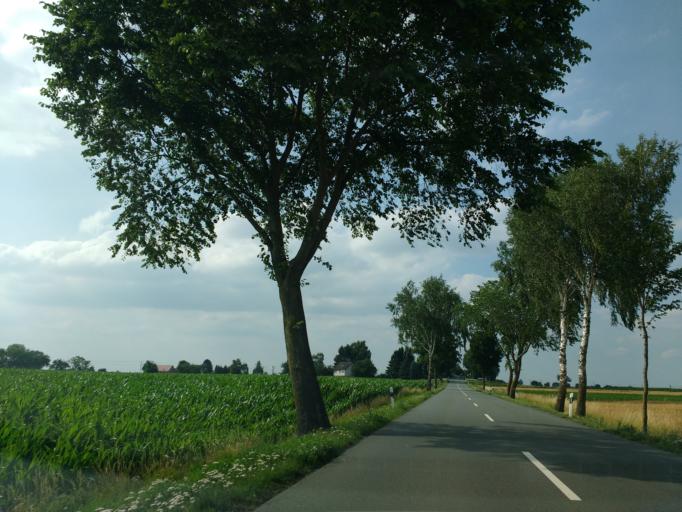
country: DE
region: North Rhine-Westphalia
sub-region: Regierungsbezirk Detmold
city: Salzkotten
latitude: 51.6847
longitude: 8.6251
